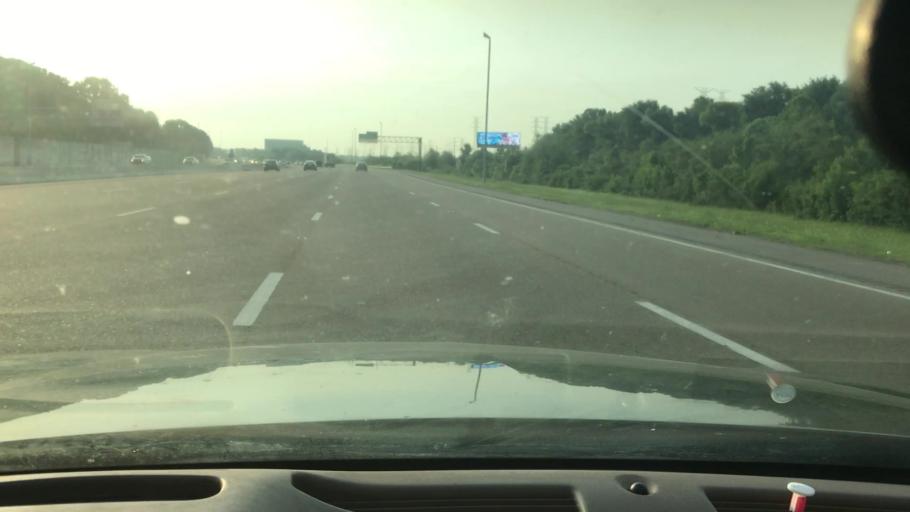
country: US
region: Tennessee
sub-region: Shelby County
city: Germantown
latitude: 35.0783
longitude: -89.9206
